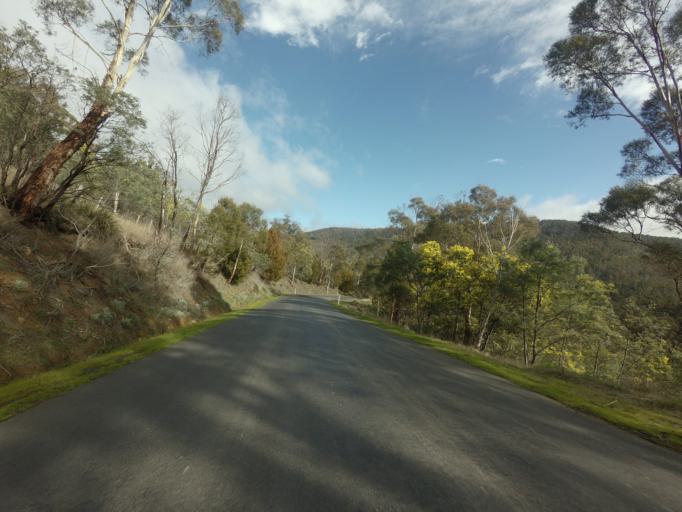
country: AU
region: Tasmania
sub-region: Derwent Valley
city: New Norfolk
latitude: -42.7809
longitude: 146.9581
